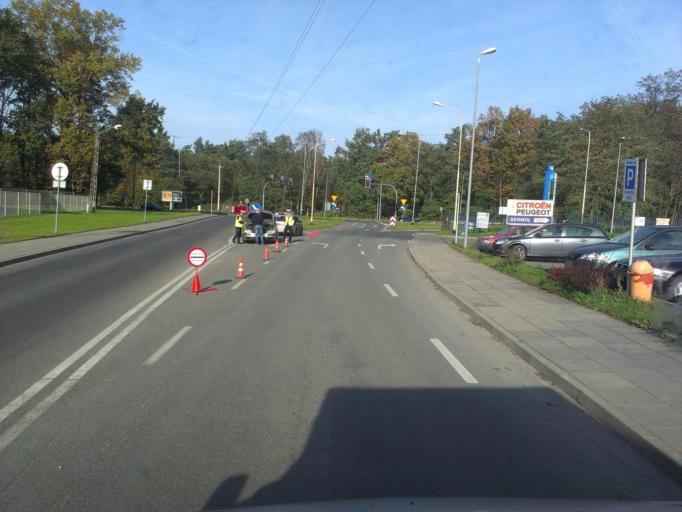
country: PL
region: West Pomeranian Voivodeship
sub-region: Powiat gryfinski
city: Stare Czarnowo
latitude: 53.3633
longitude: 14.7347
